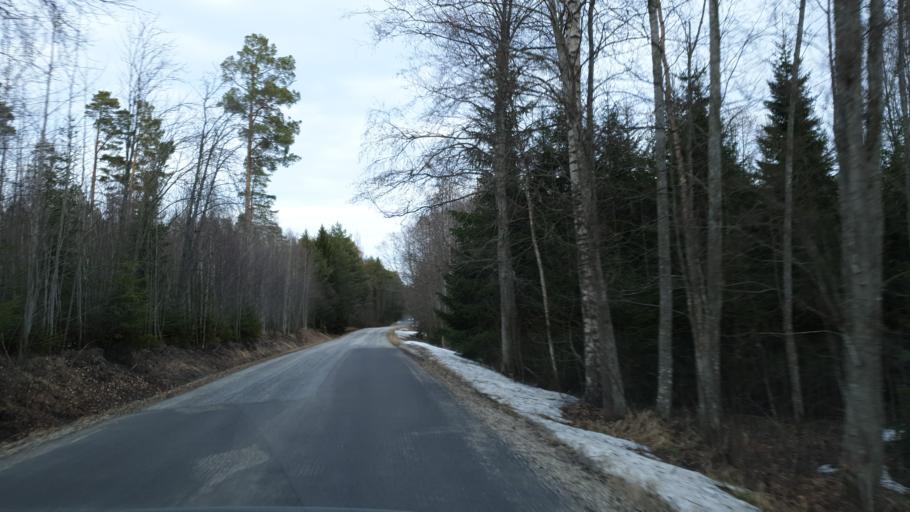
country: SE
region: Gaevleborg
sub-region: Nordanstigs Kommun
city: Bergsjoe
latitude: 61.9612
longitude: 17.3600
